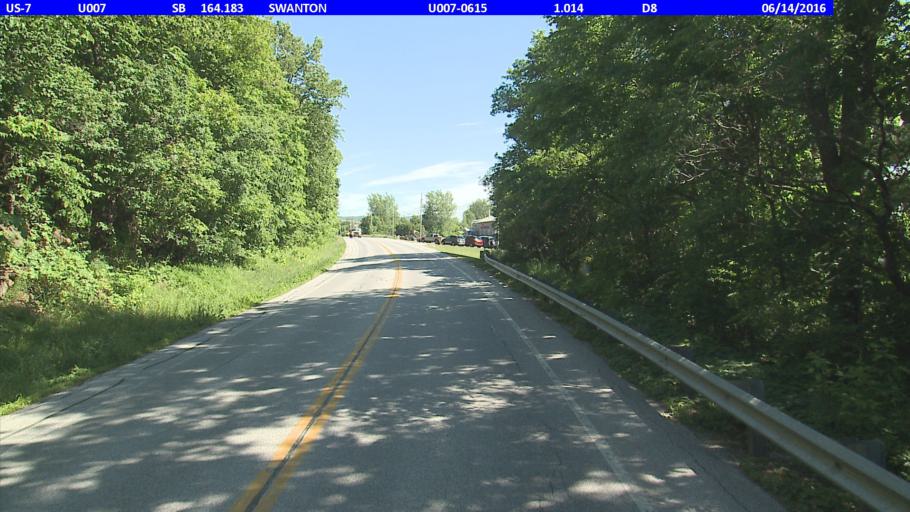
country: US
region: Vermont
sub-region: Franklin County
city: Saint Albans
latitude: 44.8623
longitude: -73.0974
